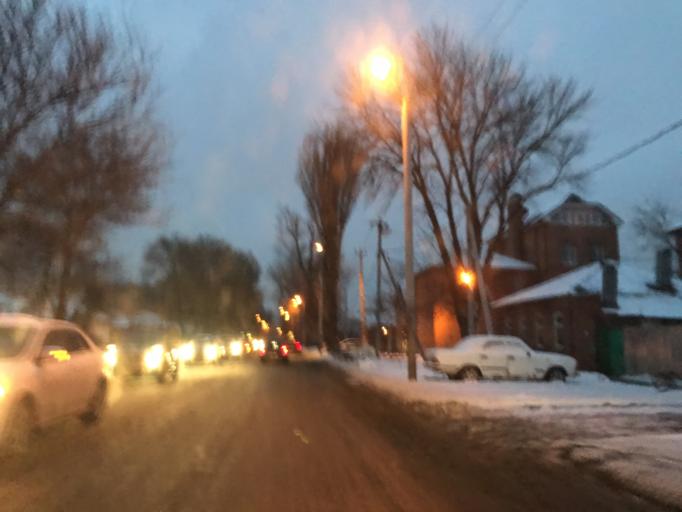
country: RU
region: Rostov
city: Imeni Chkalova
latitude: 47.2481
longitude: 39.7744
